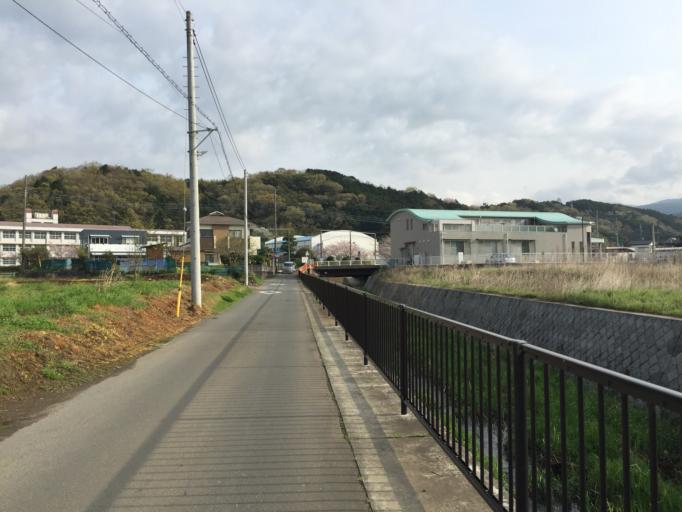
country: JP
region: Shizuoka
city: Mishima
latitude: 35.1722
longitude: 138.9222
